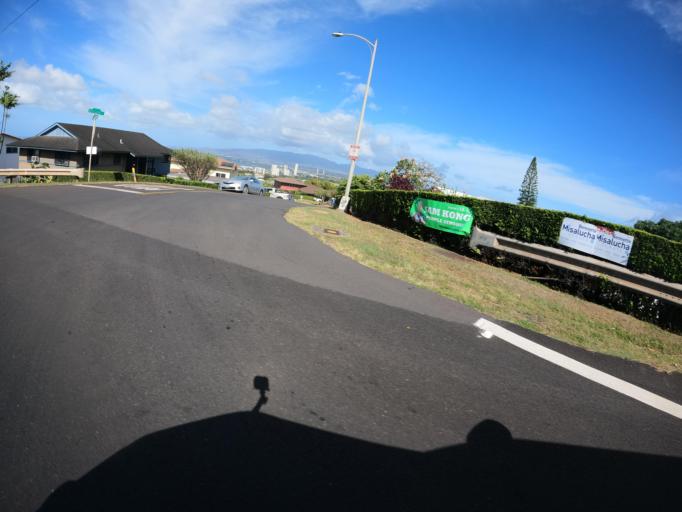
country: US
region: Hawaii
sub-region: Honolulu County
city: Halawa Heights
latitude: 21.3845
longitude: -157.9150
